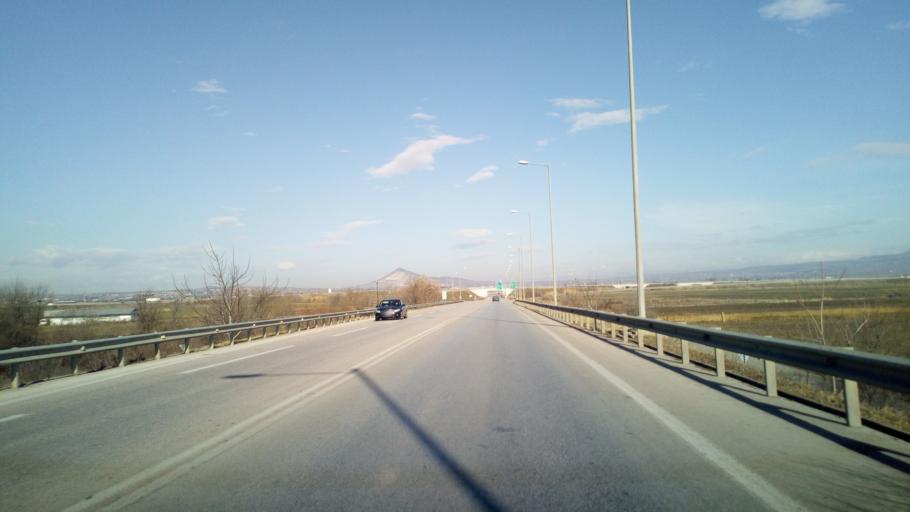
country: GR
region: Central Macedonia
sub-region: Nomos Thessalonikis
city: Lagyna
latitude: 40.7319
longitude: 23.0133
